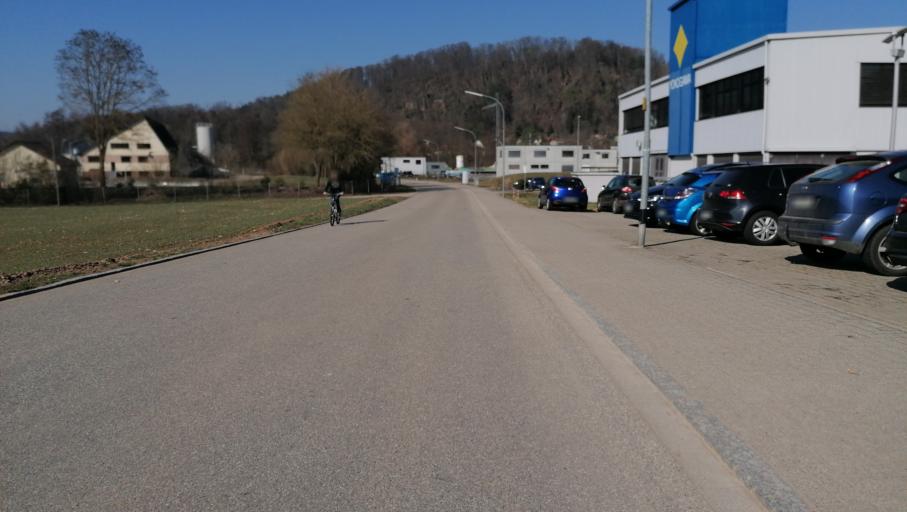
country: DE
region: Baden-Wuerttemberg
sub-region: Freiburg Region
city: Schworstadt
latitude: 47.5809
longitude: 7.9079
